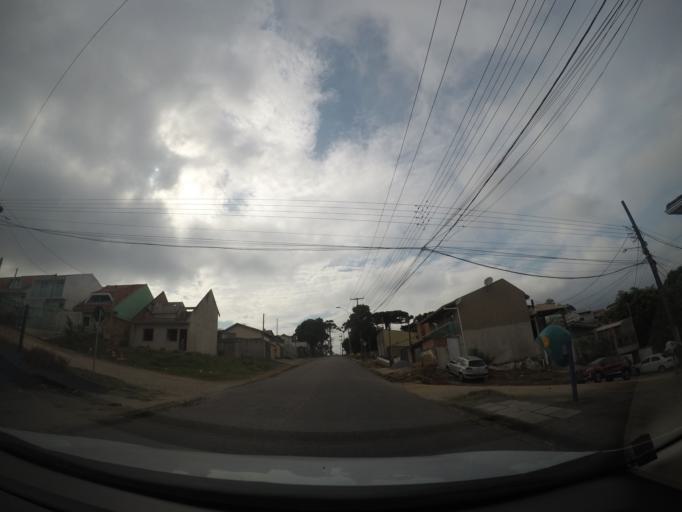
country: BR
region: Parana
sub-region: Colombo
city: Colombo
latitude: -25.3548
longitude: -49.2021
